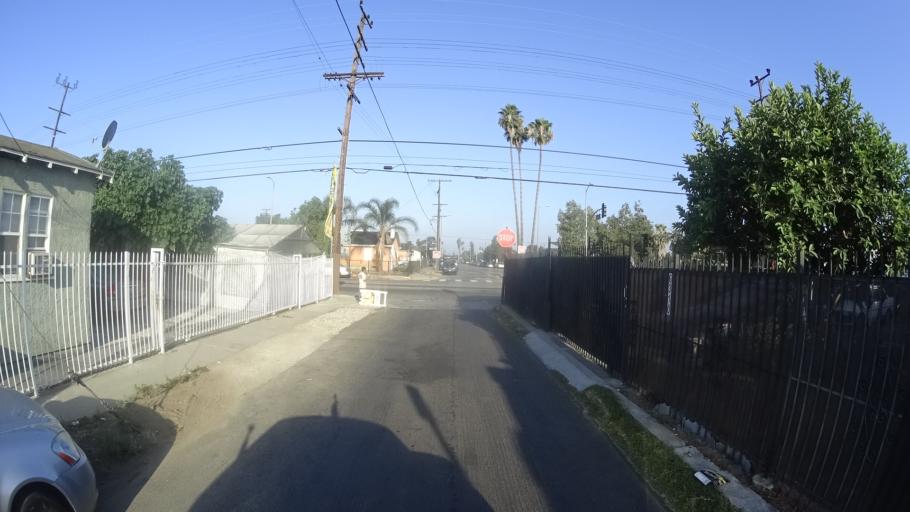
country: US
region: California
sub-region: Los Angeles County
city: Westmont
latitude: 33.9819
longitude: -118.2867
